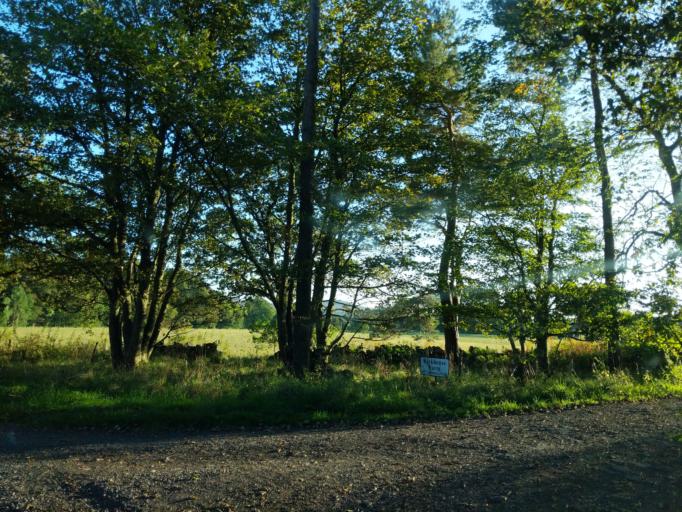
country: GB
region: Scotland
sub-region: The Scottish Borders
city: West Linton
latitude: 55.7039
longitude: -3.4352
